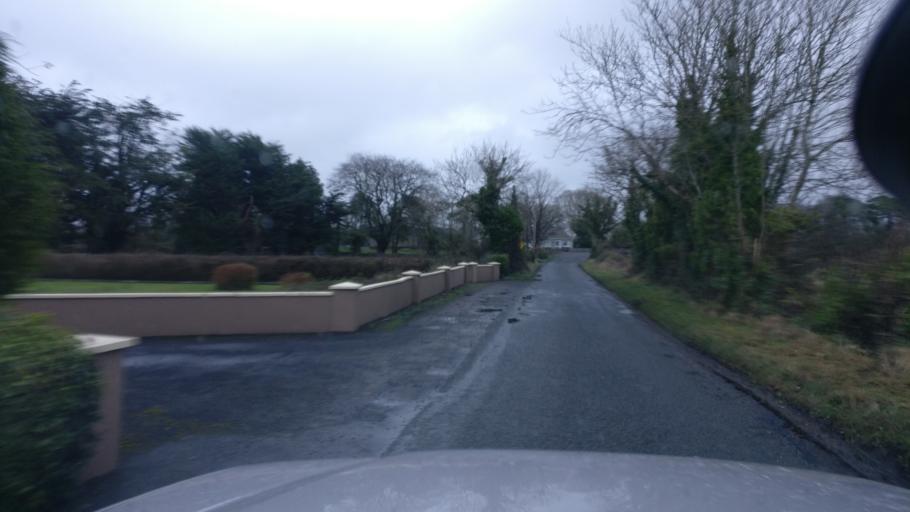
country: IE
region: Connaught
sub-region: County Galway
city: Loughrea
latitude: 53.2077
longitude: -8.6470
